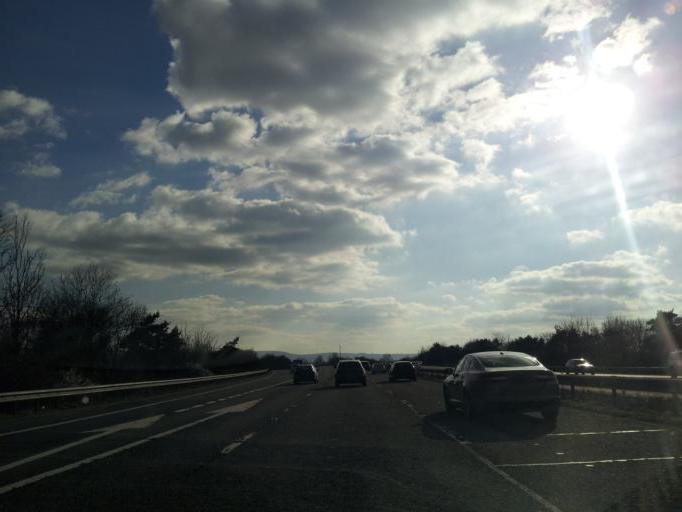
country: GB
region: England
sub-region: Somerset
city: Creech Saint Michael
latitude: 51.0213
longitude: -3.0599
